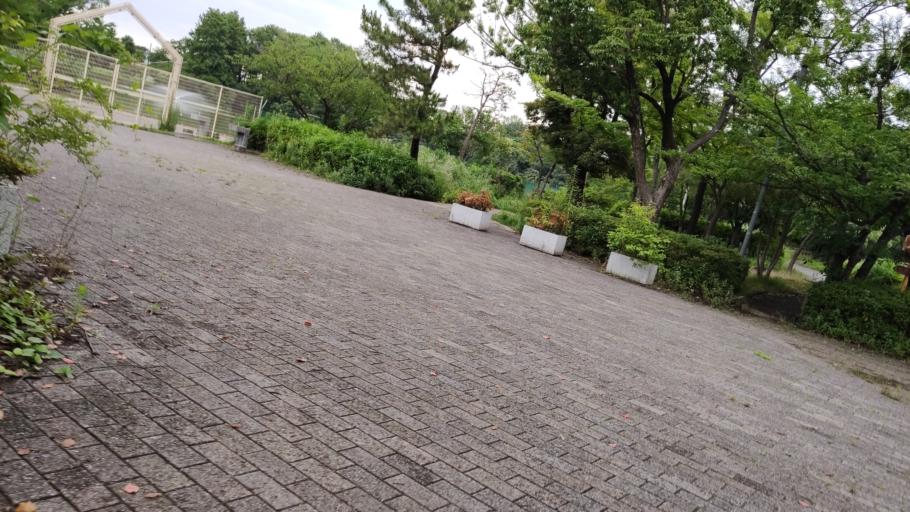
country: JP
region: Kanagawa
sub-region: Kawasaki-shi
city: Kawasaki
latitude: 35.5868
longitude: 139.6505
